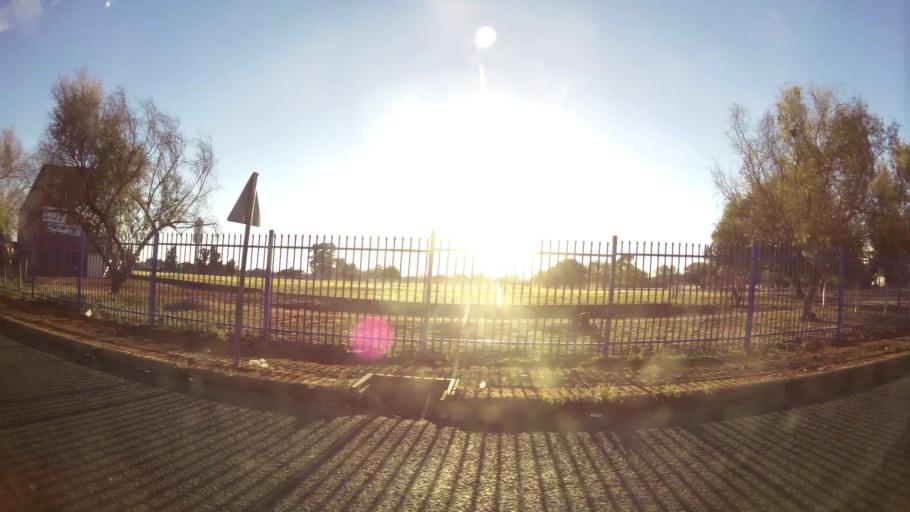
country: ZA
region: Northern Cape
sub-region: Frances Baard District Municipality
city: Kimberley
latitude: -28.7531
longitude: 24.7455
